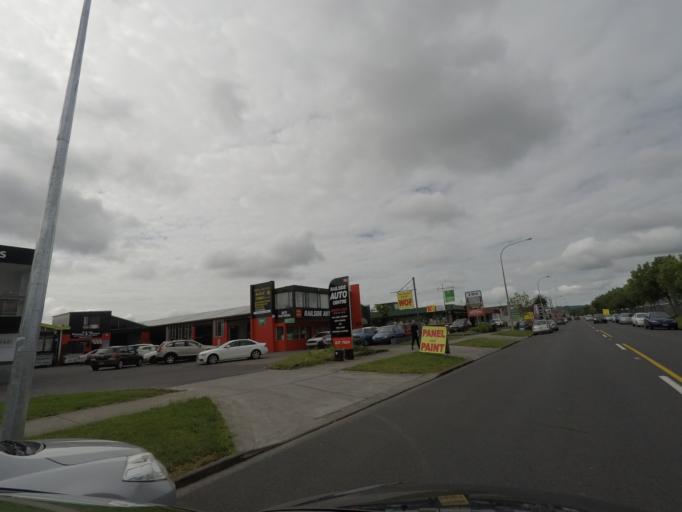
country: NZ
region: Auckland
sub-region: Auckland
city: Rosebank
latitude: -36.8864
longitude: 174.6316
